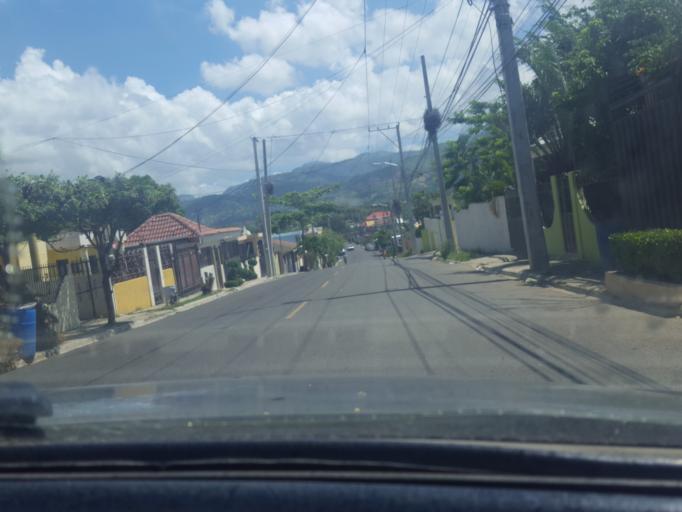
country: DO
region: Santiago
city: Santiago de los Caballeros
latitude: 19.4929
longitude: -70.6969
